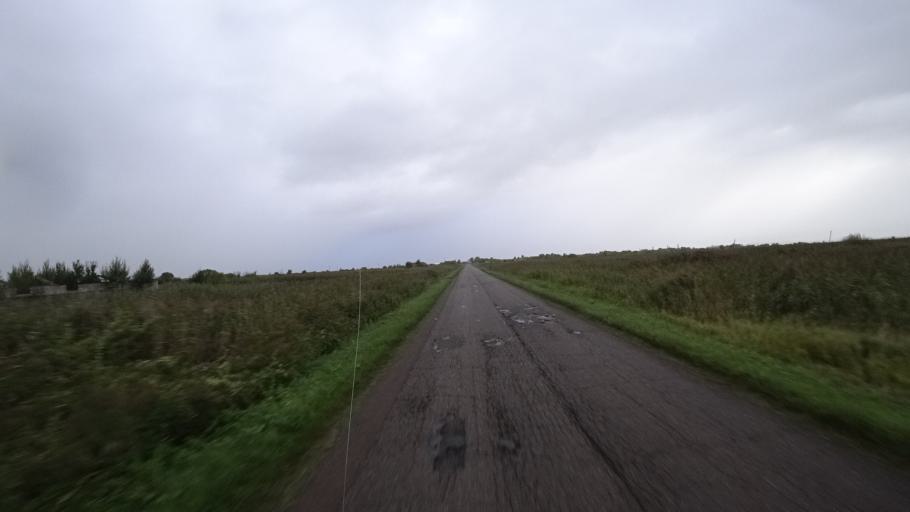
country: RU
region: Primorskiy
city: Chernigovka
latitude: 44.3909
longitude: 132.5291
